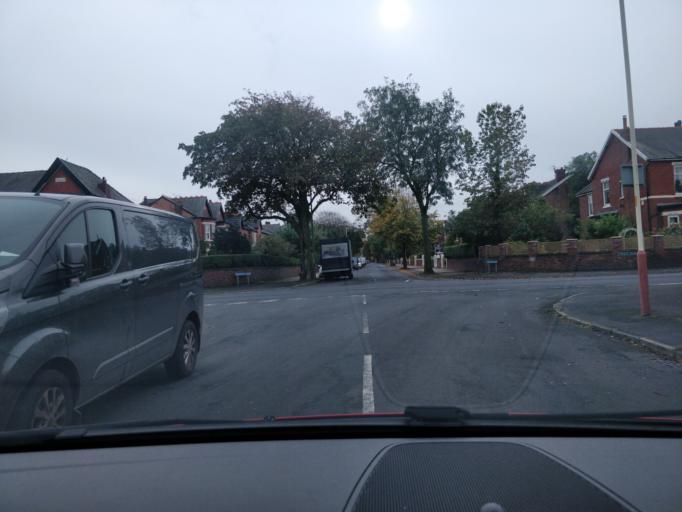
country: GB
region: England
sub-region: Sefton
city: Southport
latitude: 53.6415
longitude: -2.9849
